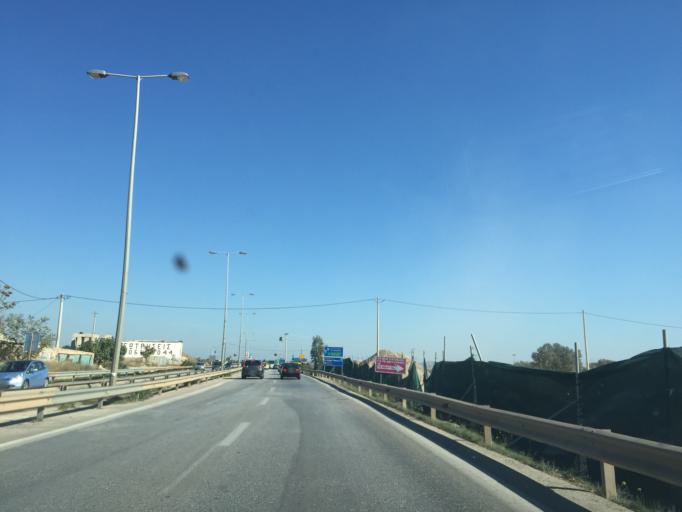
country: GR
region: Attica
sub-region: Nomarchia Anatolikis Attikis
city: Koropi
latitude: 37.9014
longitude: 23.8929
